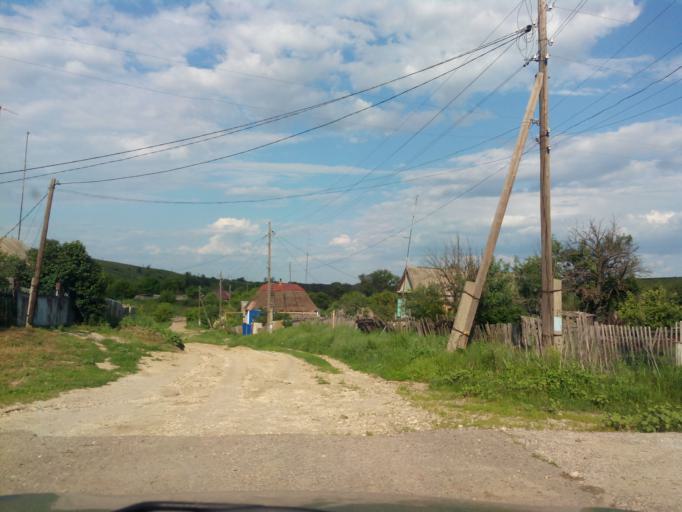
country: RU
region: Volgograd
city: Slashchevskaya
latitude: 49.7759
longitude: 42.4449
